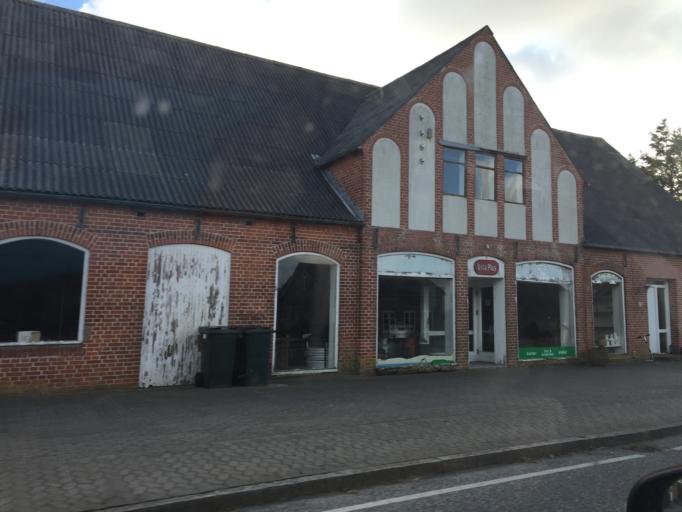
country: DK
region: South Denmark
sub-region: Tonder Kommune
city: Sherrebek
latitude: 55.0763
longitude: 8.6697
